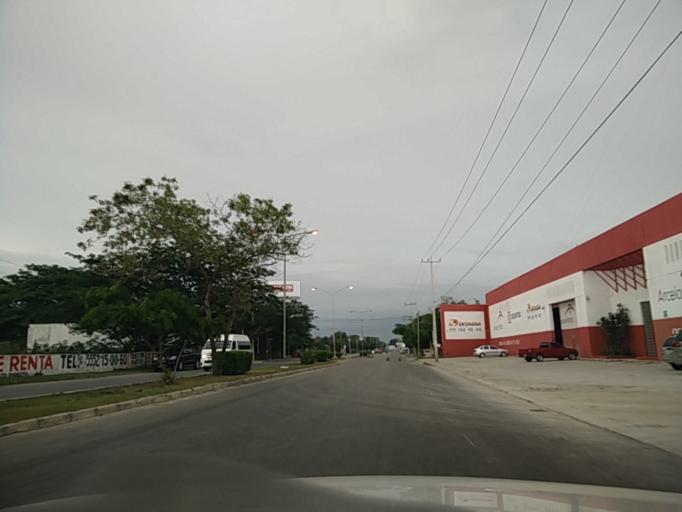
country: MX
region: Yucatan
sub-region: Kanasin
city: Kanasin
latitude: 20.9594
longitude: -89.5769
